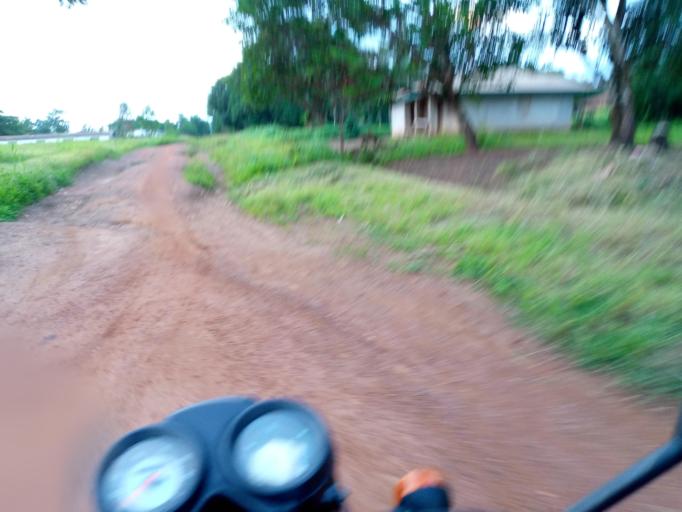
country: SL
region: Northern Province
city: Yonibana
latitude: 8.4607
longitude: -12.2187
